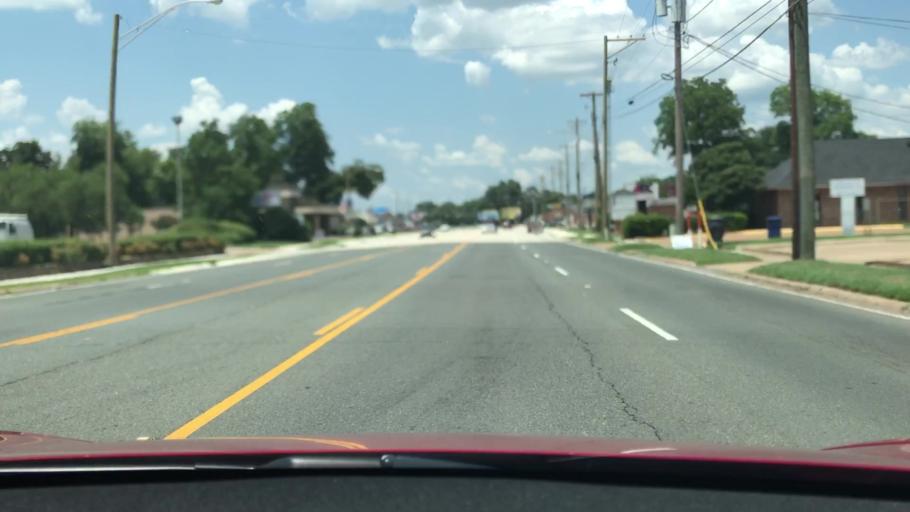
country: US
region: Louisiana
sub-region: Bossier Parish
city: Bossier City
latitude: 32.4767
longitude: -93.7221
